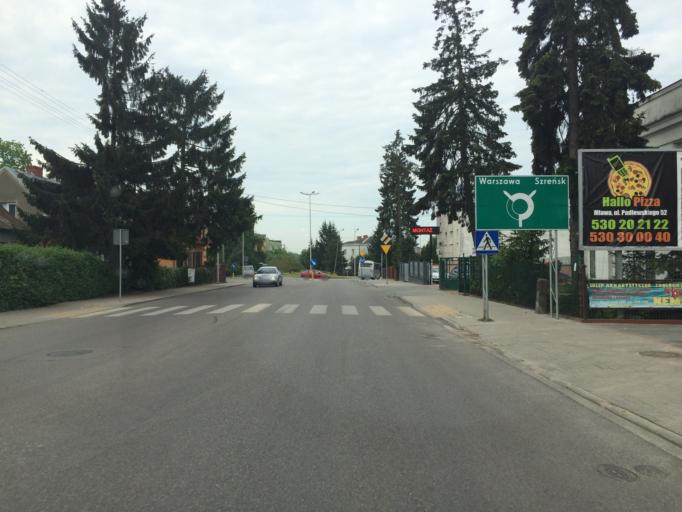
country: PL
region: Masovian Voivodeship
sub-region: Powiat mlawski
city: Mlawa
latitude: 53.1095
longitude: 20.3734
